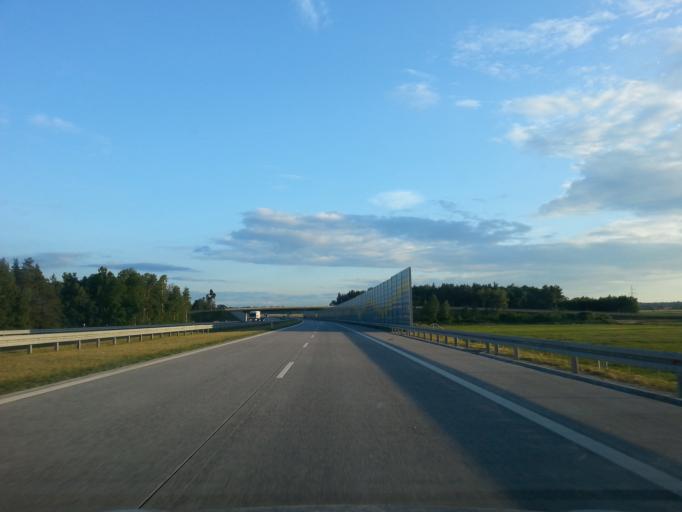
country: PL
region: Lodz Voivodeship
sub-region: Powiat sieradzki
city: Brzeznio
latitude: 51.4587
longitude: 18.6511
